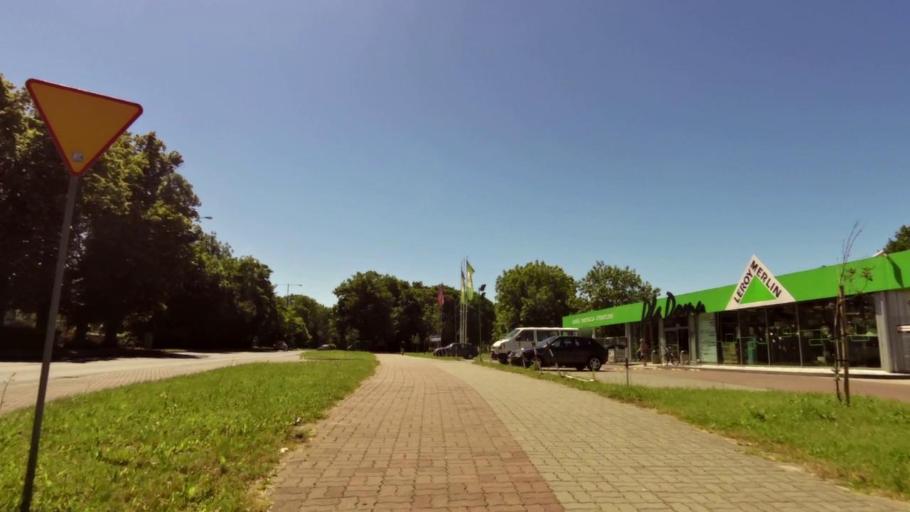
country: PL
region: West Pomeranian Voivodeship
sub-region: Powiat kolobrzeski
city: Kolobrzeg
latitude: 54.1597
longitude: 15.5658
